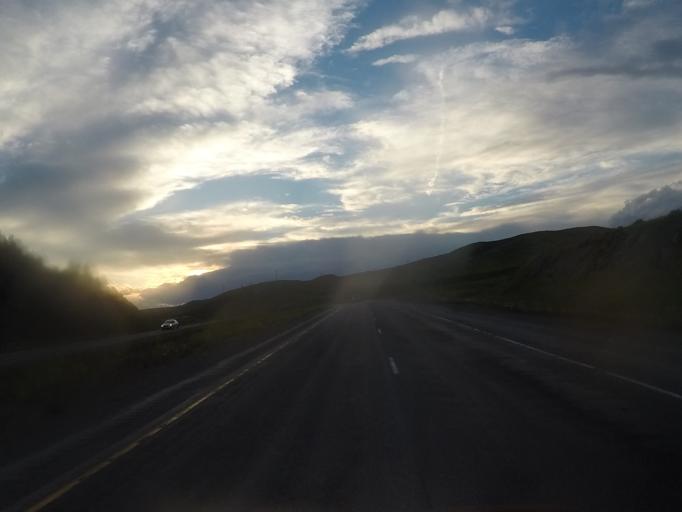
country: US
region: Montana
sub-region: Gallatin County
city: Bozeman
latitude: 45.6655
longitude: -110.8021
